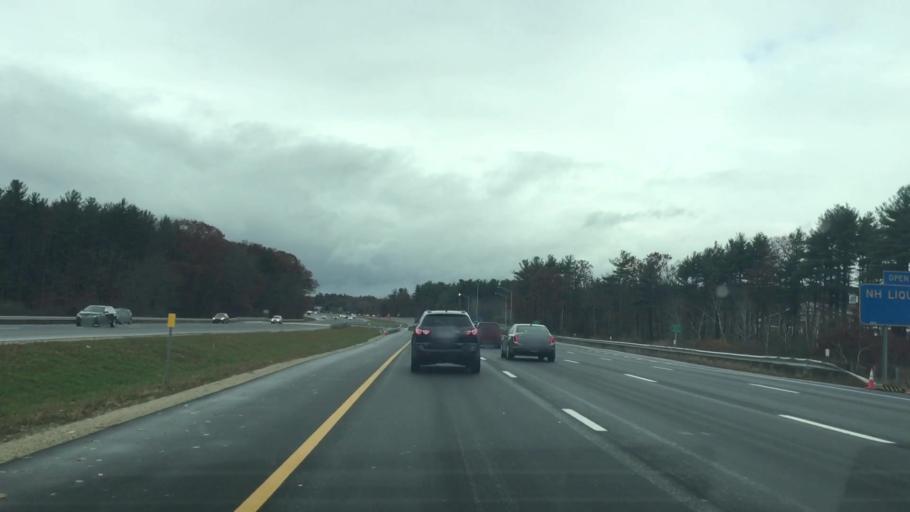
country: US
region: New Hampshire
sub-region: Rockingham County
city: Hampton Falls
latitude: 42.9320
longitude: -70.8636
